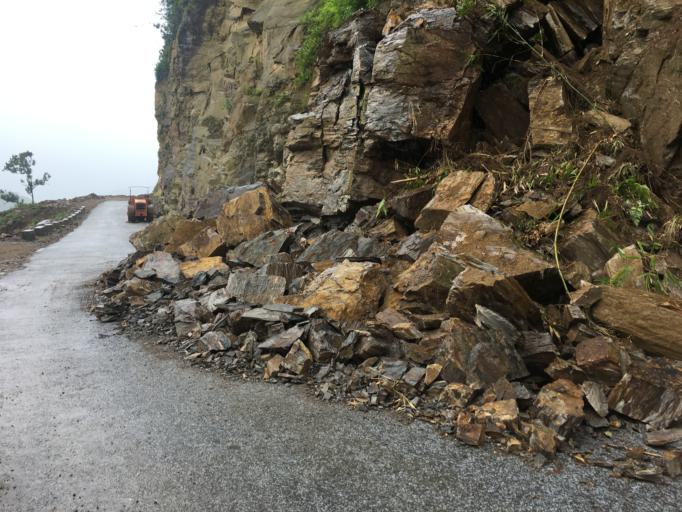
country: VN
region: Ha Giang
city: Thi Tran Tam Son
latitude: 22.9852
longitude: 105.0633
